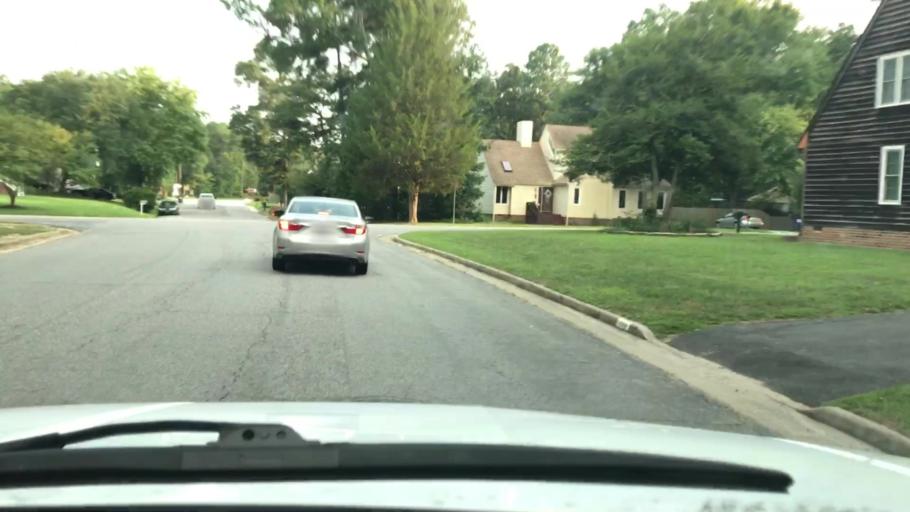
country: US
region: Virginia
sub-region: Chesterfield County
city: Chesterfield
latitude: 37.4370
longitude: -77.5173
